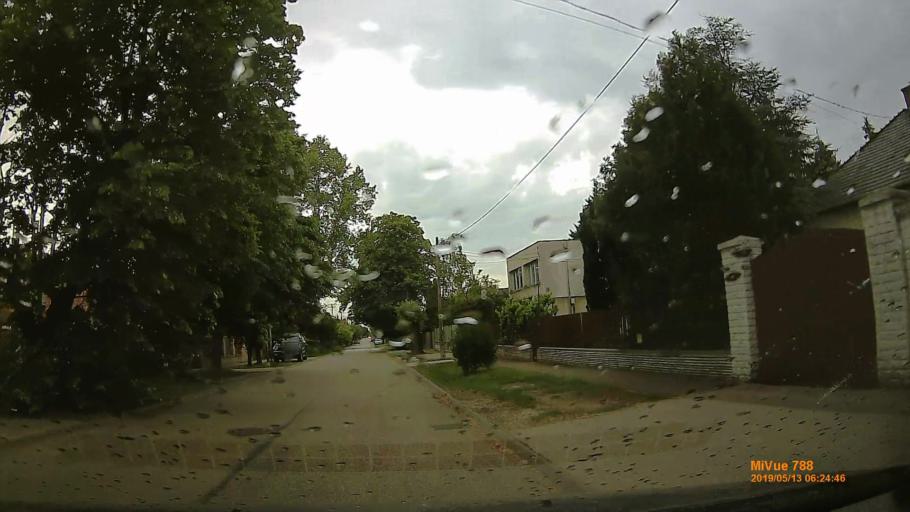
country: HU
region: Budapest
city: Budapest XXI. keruelet
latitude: 47.4255
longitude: 19.0826
